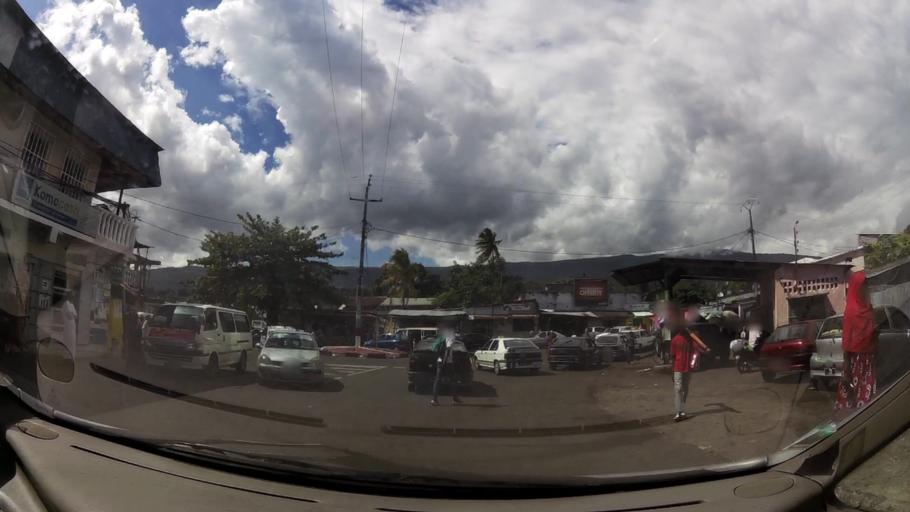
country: KM
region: Grande Comore
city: Mavingouni
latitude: -11.7101
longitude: 43.2521
